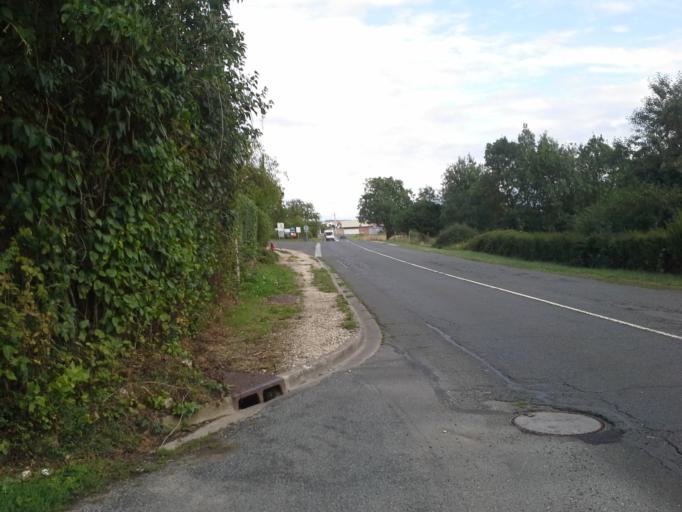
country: FR
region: Centre
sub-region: Departement du Loir-et-Cher
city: Villiers-sur-Loir
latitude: 47.8113
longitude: 0.9779
